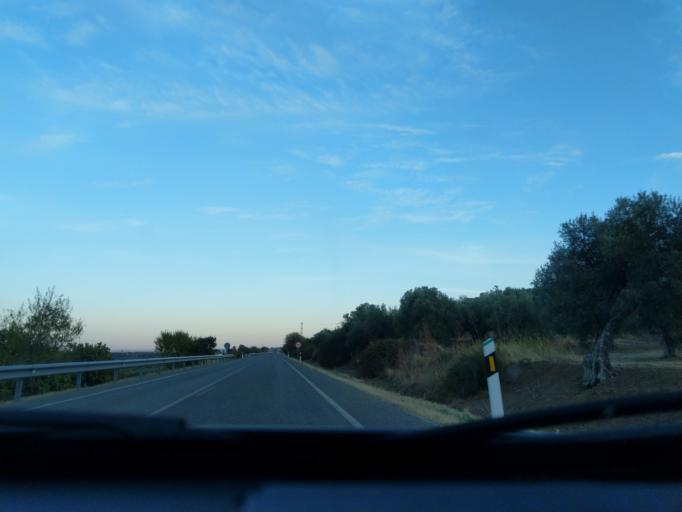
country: ES
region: Extremadura
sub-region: Provincia de Badajoz
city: Reina
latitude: 38.1873
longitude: -5.9405
